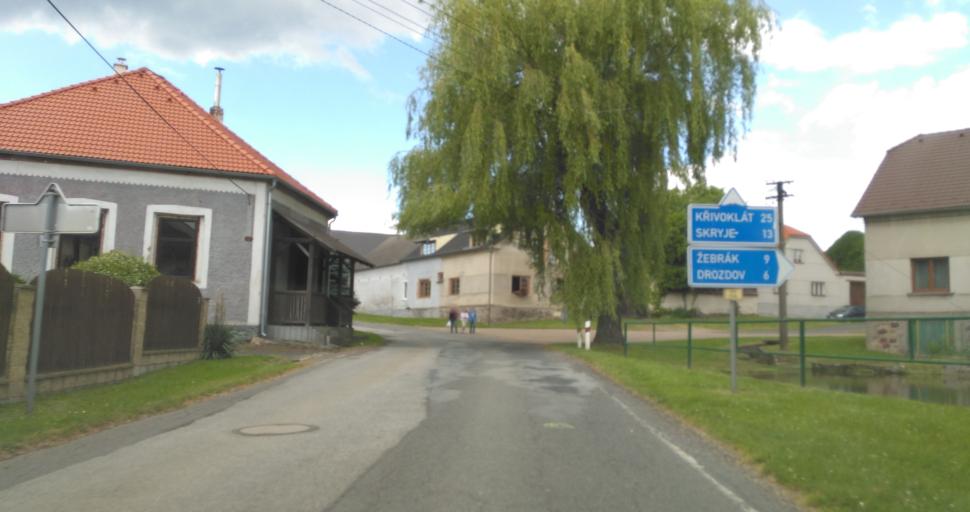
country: CZ
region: Plzensky
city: Zbiroh
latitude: 49.8848
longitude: 13.8047
